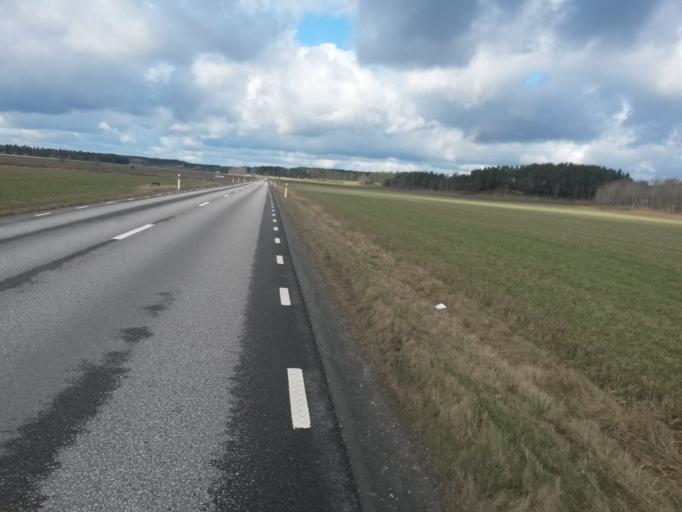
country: SE
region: Vaestra Goetaland
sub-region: Vargarda Kommun
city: Vargarda
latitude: 58.0441
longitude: 12.7938
